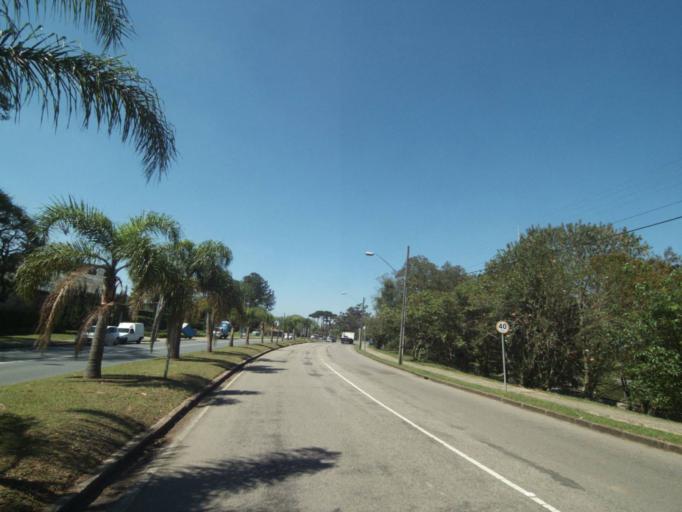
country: BR
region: Parana
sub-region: Curitiba
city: Curitiba
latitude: -25.4124
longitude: -49.2409
